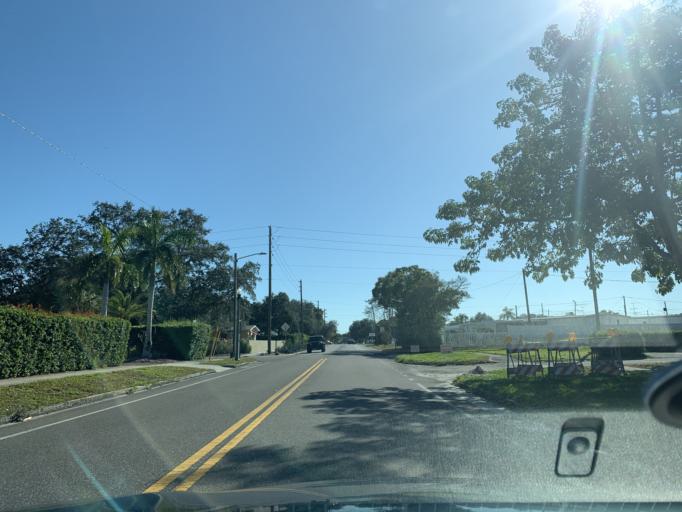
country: US
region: Florida
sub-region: Pinellas County
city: South Pasadena
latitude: 27.7633
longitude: -82.7243
